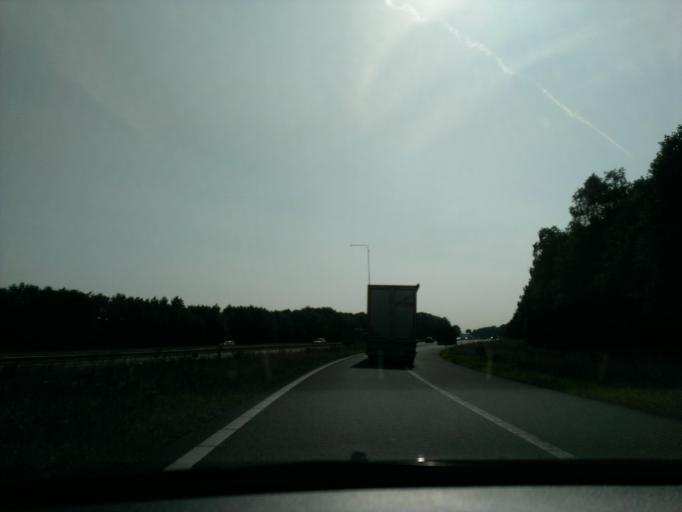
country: NL
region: Overijssel
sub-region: Gemeente Hof van Twente
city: Delden
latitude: 52.3098
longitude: 6.6910
